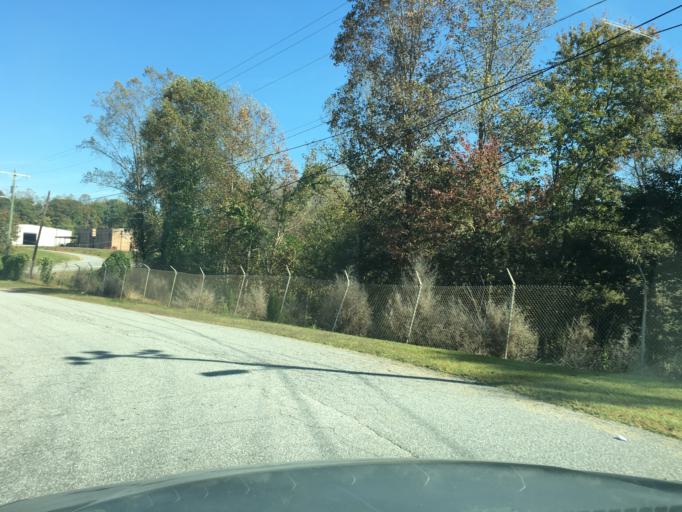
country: US
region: North Carolina
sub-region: Catawba County
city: Conover
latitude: 35.7117
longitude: -81.2448
